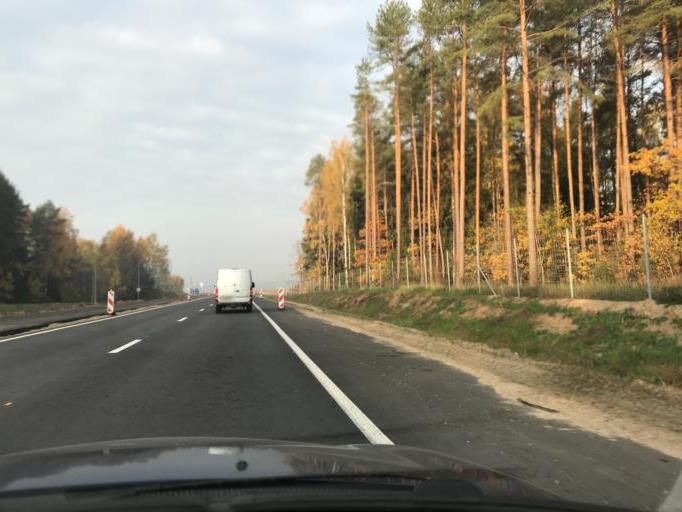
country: BY
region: Grodnenskaya
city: Lida
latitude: 53.8293
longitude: 25.3827
